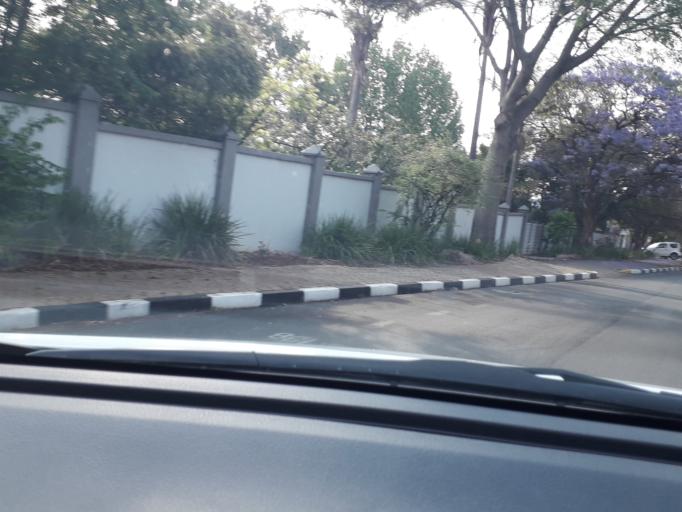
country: ZA
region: Gauteng
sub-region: City of Johannesburg Metropolitan Municipality
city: Johannesburg
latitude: -26.1298
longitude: 27.9929
